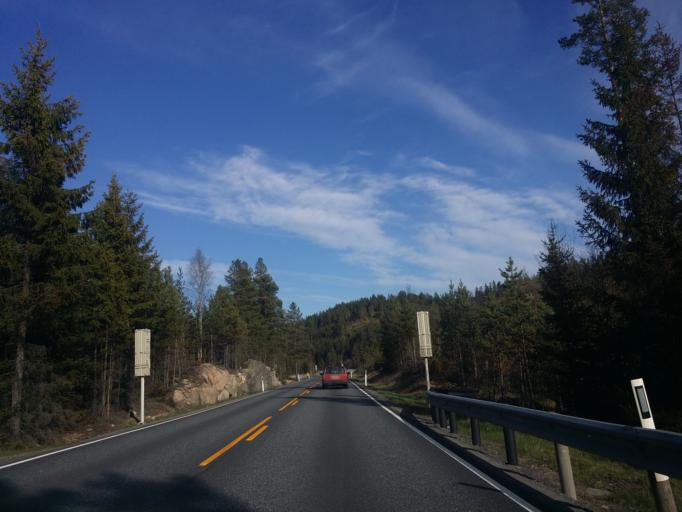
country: NO
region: Buskerud
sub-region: Kongsberg
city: Kongsberg
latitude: 59.6321
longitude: 9.5249
